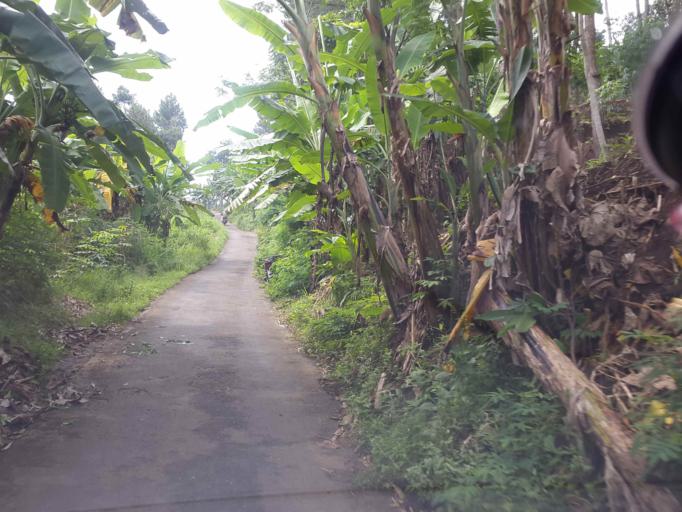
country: ID
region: Central Java
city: Baturaden
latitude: -7.2743
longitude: 109.0516
